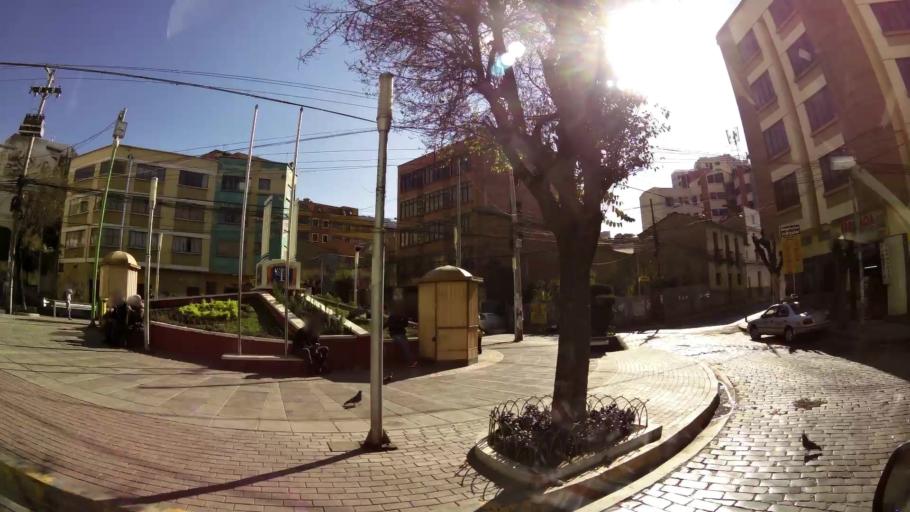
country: BO
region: La Paz
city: La Paz
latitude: -16.5054
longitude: -68.1365
